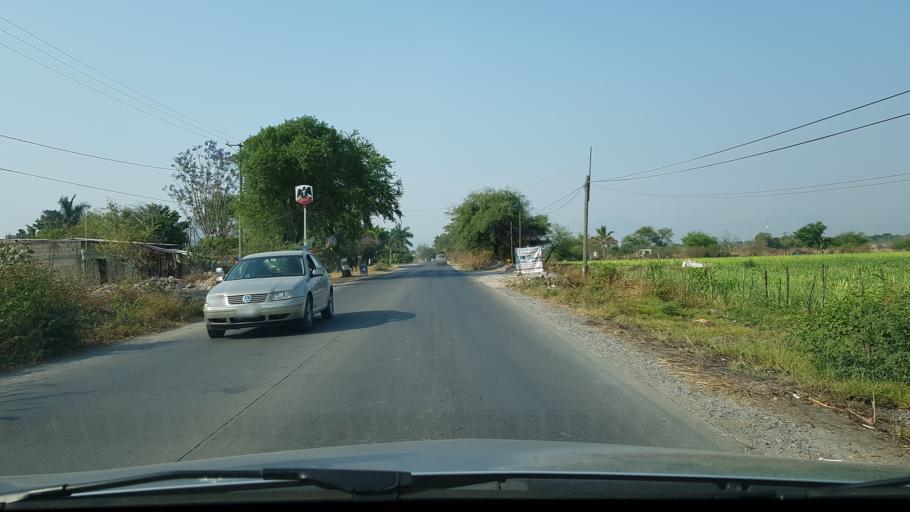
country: MX
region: Morelos
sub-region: Tlaquiltenango
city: Alfredo V. Bonfil (Chacampalco)
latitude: 18.6673
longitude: -99.1471
